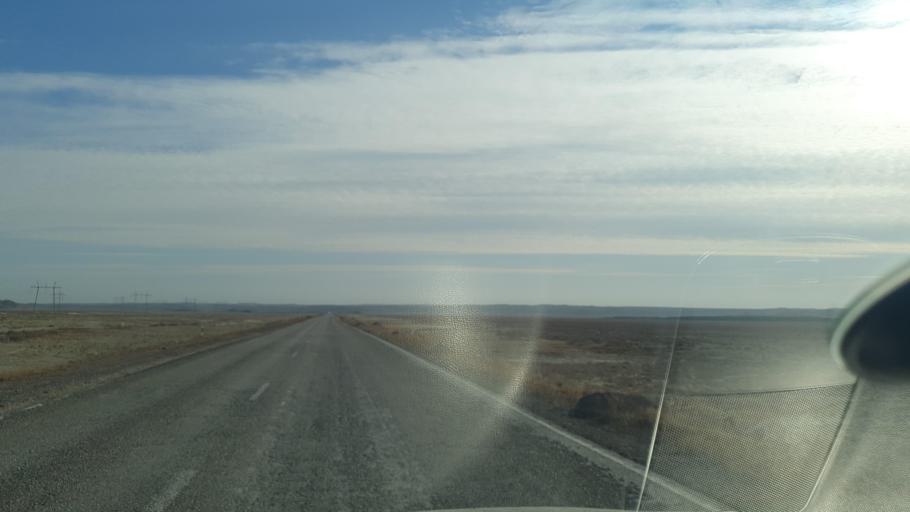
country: KZ
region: Zhambyl
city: Mynaral
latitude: 45.5814
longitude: 73.4085
